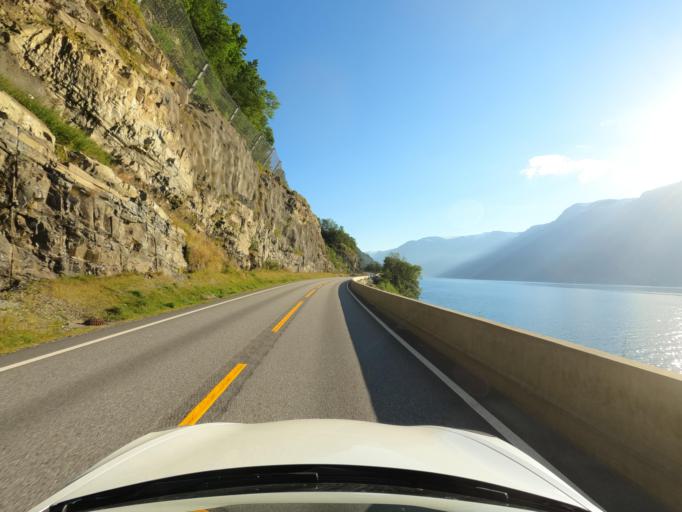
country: NO
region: Hordaland
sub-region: Ullensvang
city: Kinsarvik
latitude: 60.3047
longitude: 6.6441
